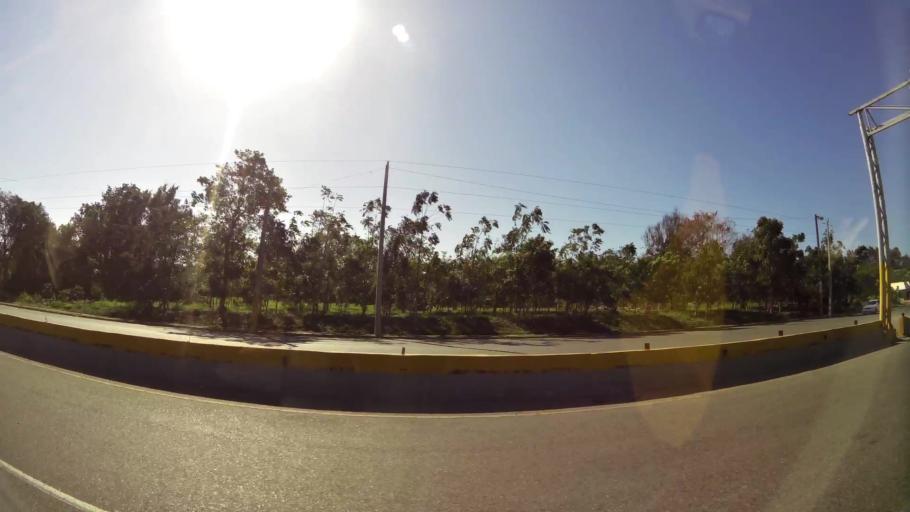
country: DO
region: San Cristobal
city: El Carril
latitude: 18.4443
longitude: -70.0005
